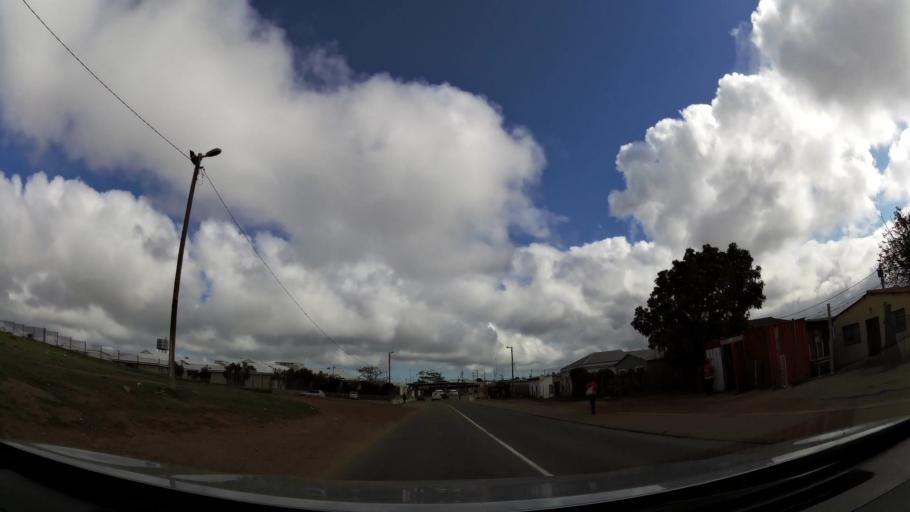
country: ZA
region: Western Cape
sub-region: Eden District Municipality
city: Plettenberg Bay
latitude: -34.0523
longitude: 23.3204
